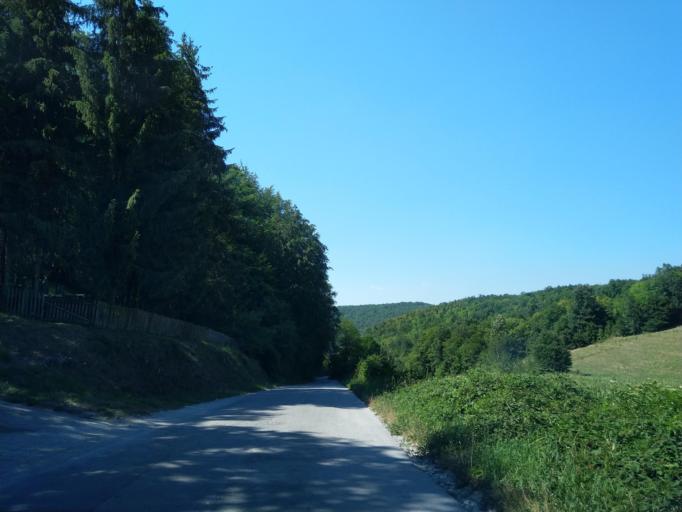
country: RS
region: Central Serbia
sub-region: Zlatiborski Okrug
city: Uzice
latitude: 43.8238
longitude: 19.8571
